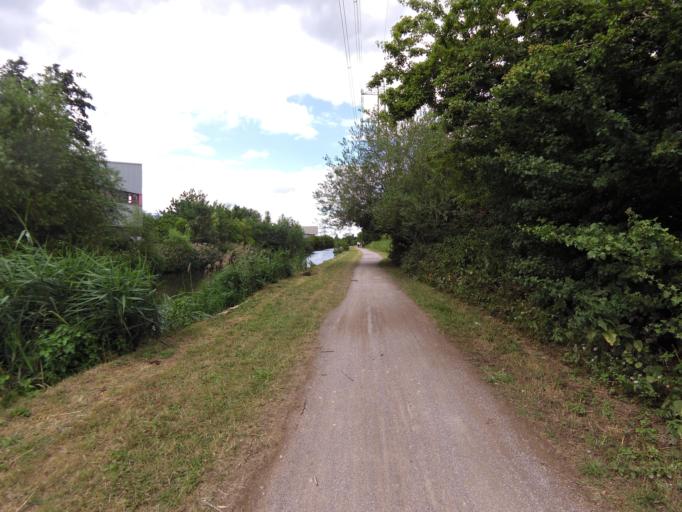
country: GB
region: England
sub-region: Essex
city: Waltham Abbey
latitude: 51.6577
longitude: -0.0202
